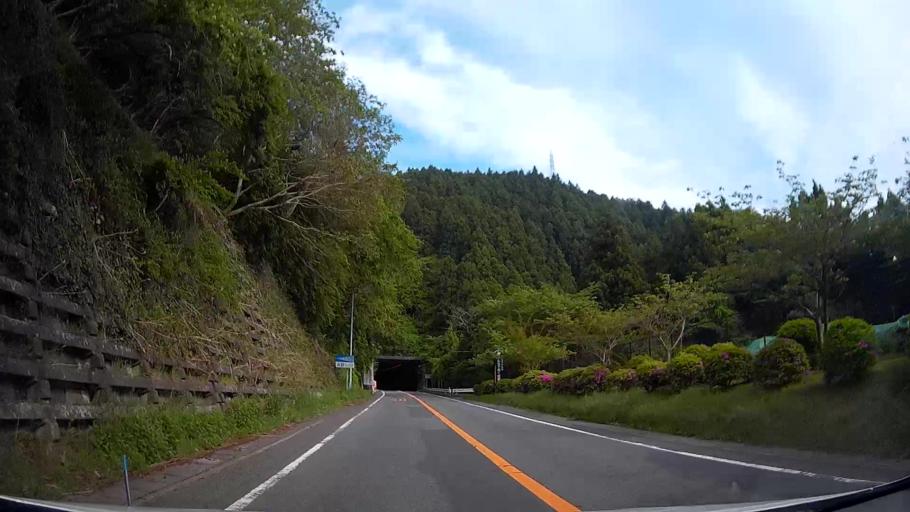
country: JP
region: Shizuoka
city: Heda
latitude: 34.9225
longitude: 138.8356
